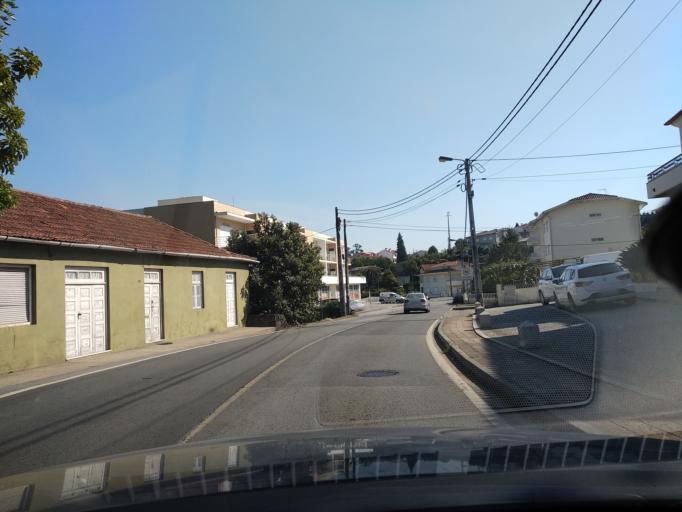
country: PT
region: Porto
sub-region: Paredes
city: Madalena
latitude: 41.2253
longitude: -8.3619
